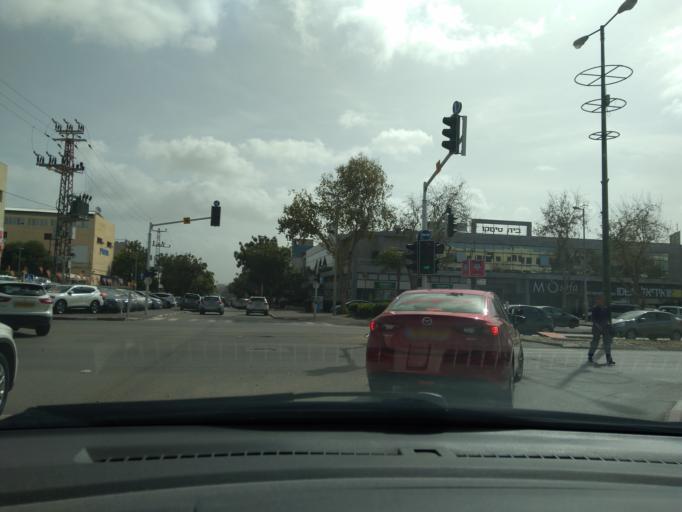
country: IL
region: Central District
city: Even Yehuda
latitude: 32.2805
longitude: 34.8607
